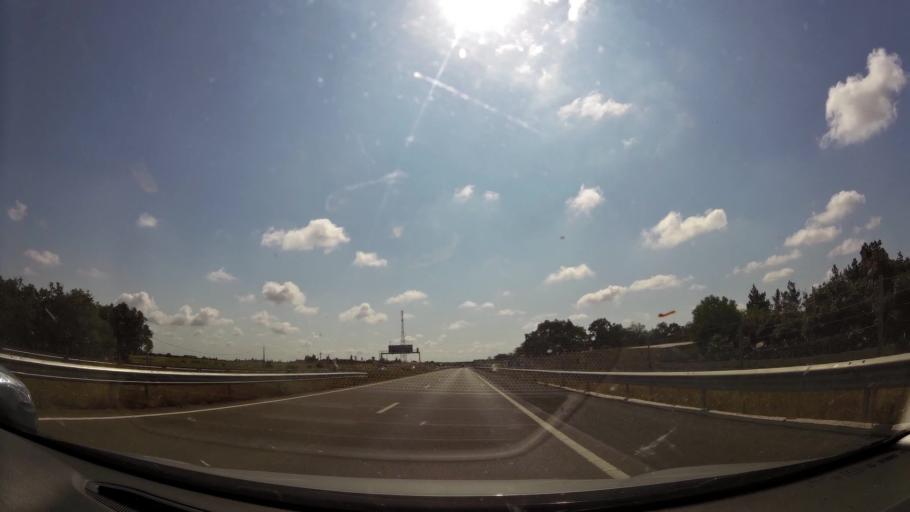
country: MA
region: Rabat-Sale-Zemmour-Zaer
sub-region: Skhirate-Temara
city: Temara
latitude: 33.8405
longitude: -6.8587
